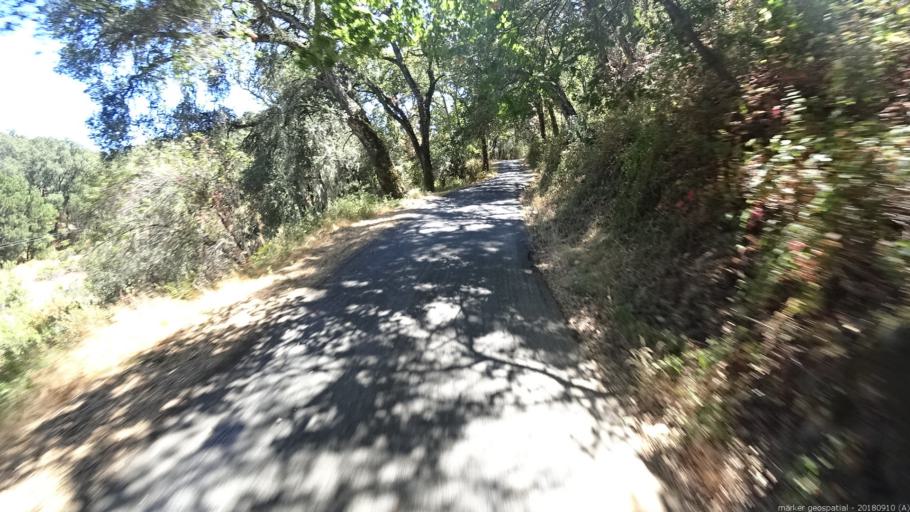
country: US
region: California
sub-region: Monterey County
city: Carmel Valley Village
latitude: 36.4322
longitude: -121.7906
